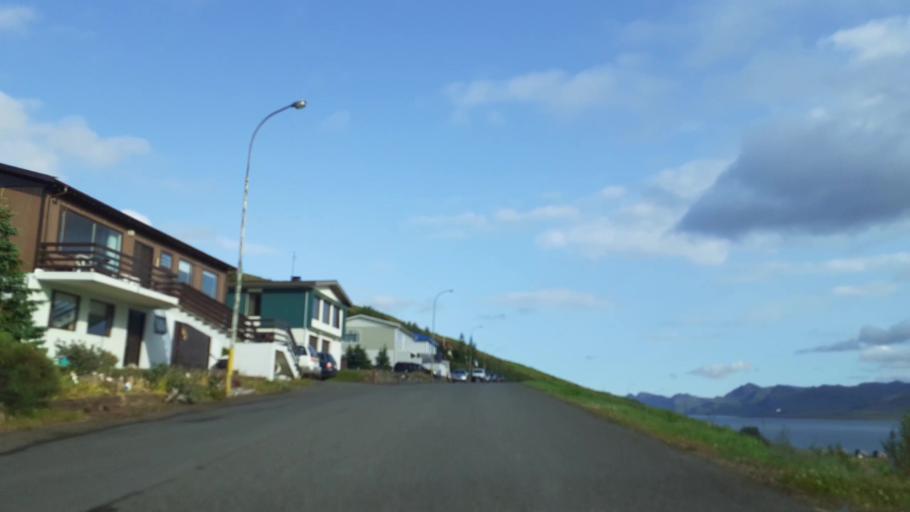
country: IS
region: East
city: Eskifjoerdur
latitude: 65.0656
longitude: -13.9977
